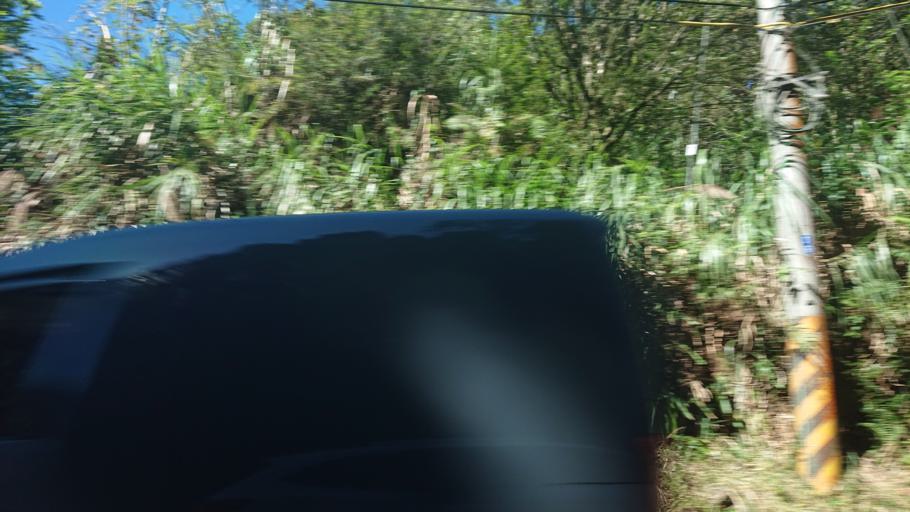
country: TW
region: Taiwan
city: Lugu
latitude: 23.4946
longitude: 120.7939
